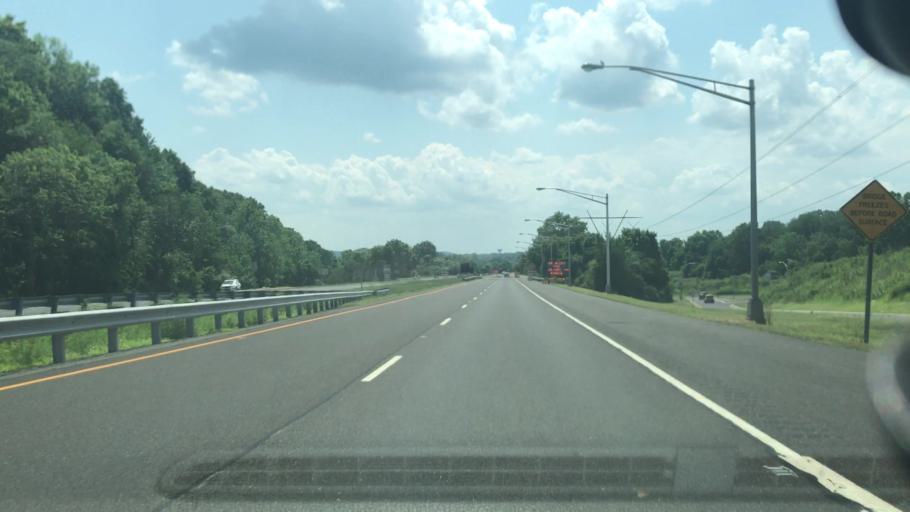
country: US
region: New Jersey
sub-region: Hunterdon County
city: Lambertville
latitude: 40.3850
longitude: -74.9445
